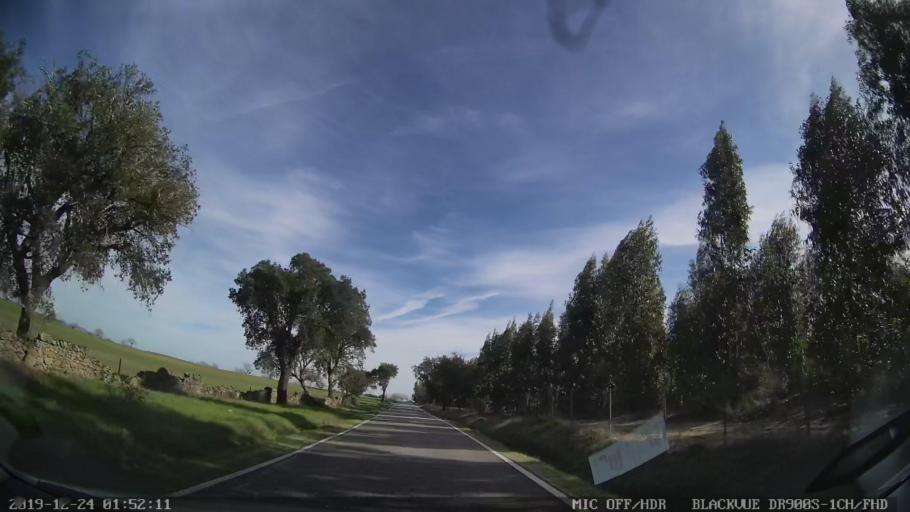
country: PT
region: Portalegre
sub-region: Nisa
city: Nisa
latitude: 39.4930
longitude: -7.7486
